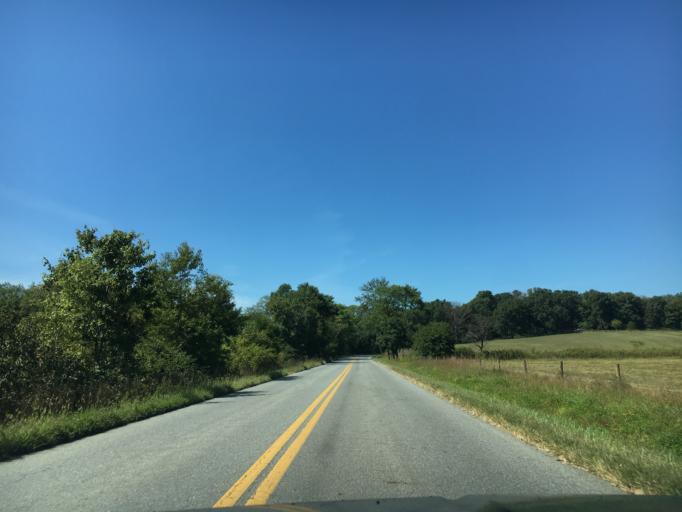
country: US
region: Virginia
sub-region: Albemarle County
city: Crozet
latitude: 37.9583
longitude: -78.6627
